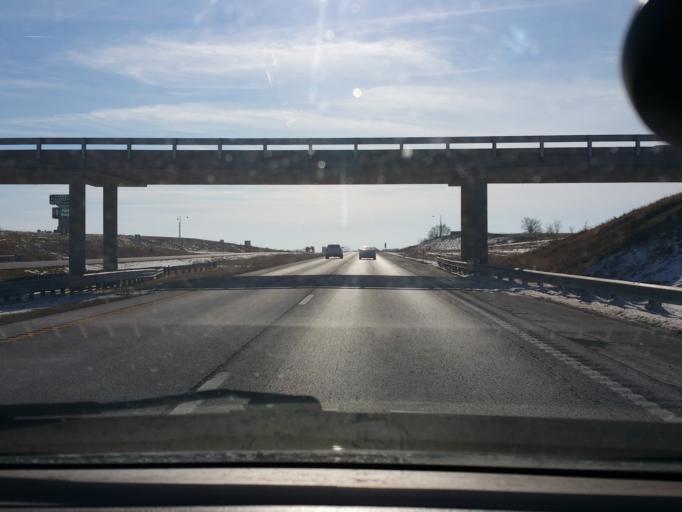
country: US
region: Missouri
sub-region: Clinton County
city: Cameron
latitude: 39.7320
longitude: -94.2207
